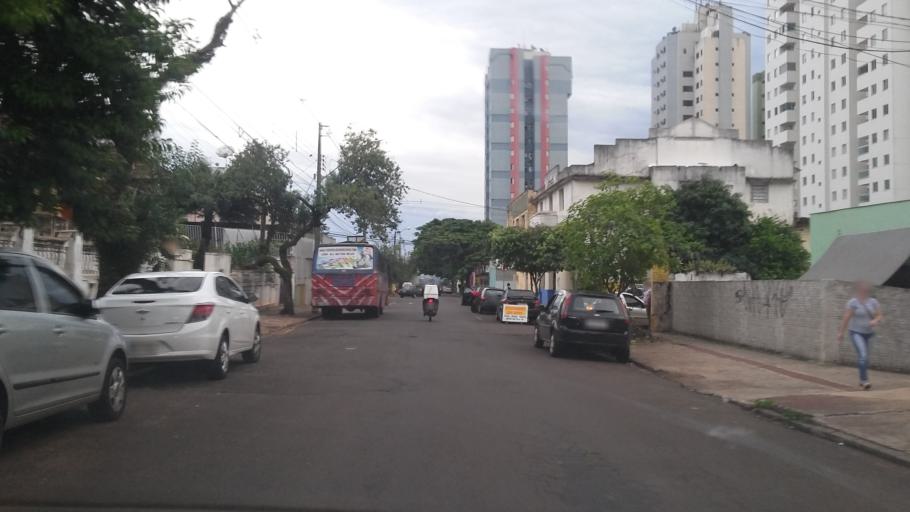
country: BR
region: Parana
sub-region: Londrina
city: Londrina
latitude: -23.3074
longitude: -51.1654
